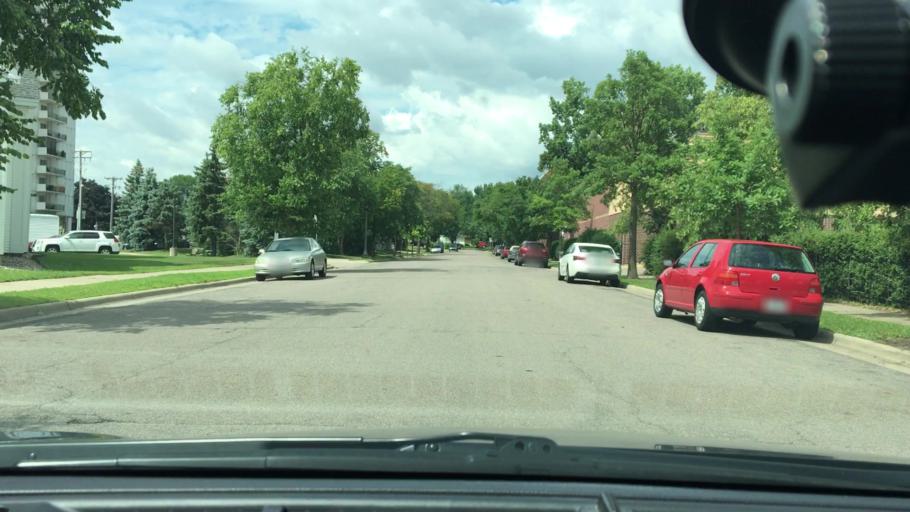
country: US
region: Minnesota
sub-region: Dakota County
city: Mendota Heights
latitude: 44.9182
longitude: -93.1969
